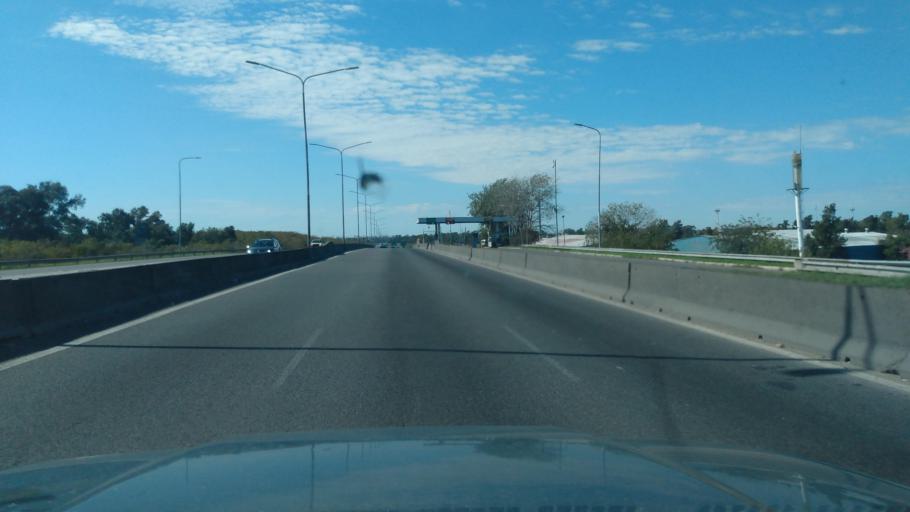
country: AR
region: Buenos Aires
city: Hurlingham
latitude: -34.5686
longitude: -58.6509
